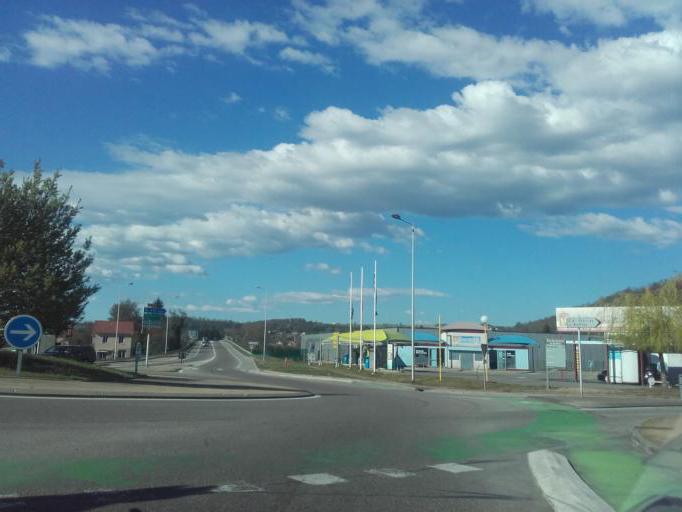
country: FR
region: Rhone-Alpes
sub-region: Departement de l'Isere
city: Nivolas-Vermelle
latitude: 45.5734
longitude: 5.3017
